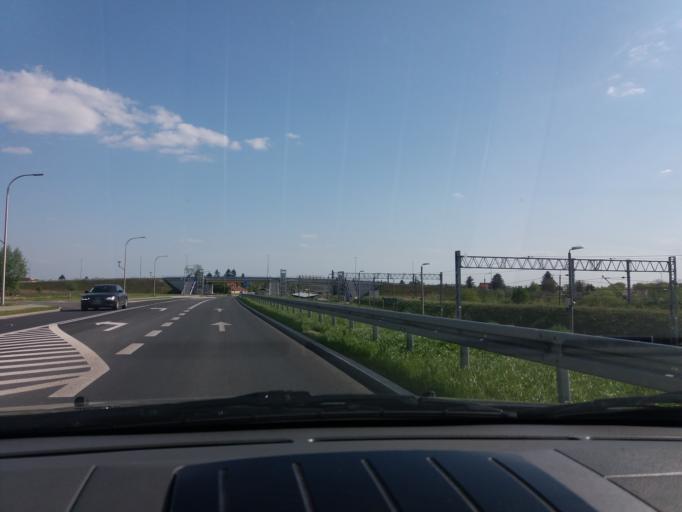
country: PL
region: Masovian Voivodeship
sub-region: Powiat mlawski
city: Mlawa
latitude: 53.1107
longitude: 20.3632
